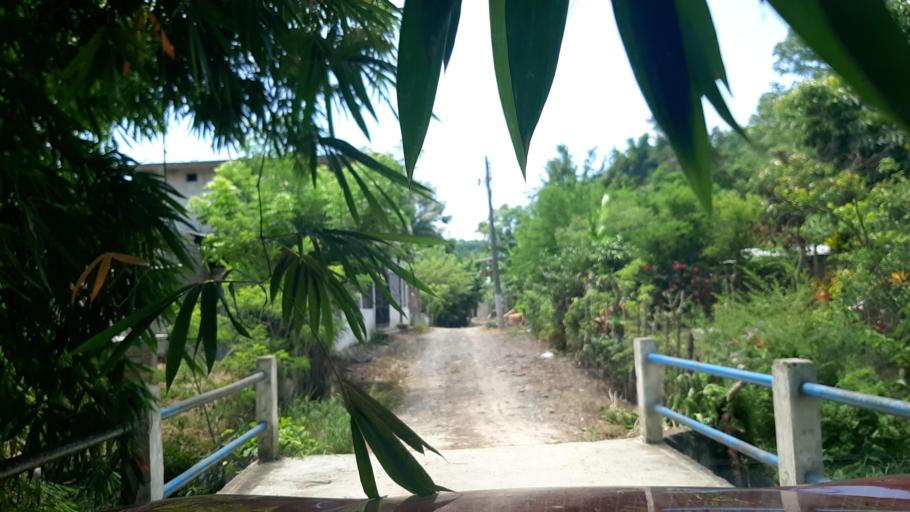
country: MX
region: Veracruz
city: Cazones de Herrera
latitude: 20.6783
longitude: -97.3214
